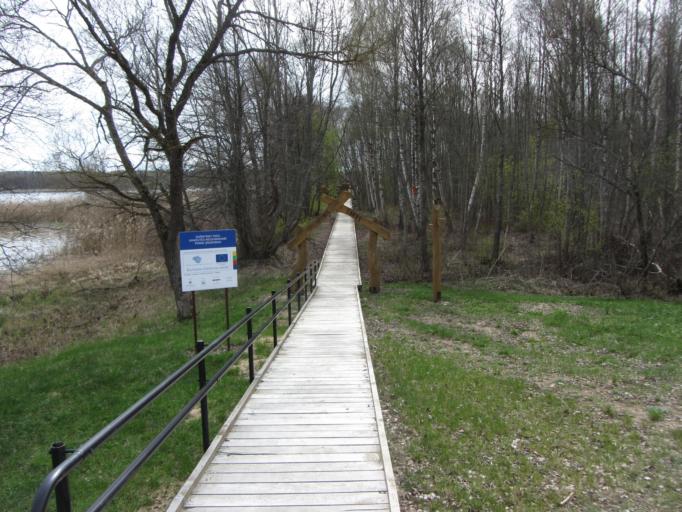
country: LT
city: Zarasai
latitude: 55.5810
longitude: 26.1559
